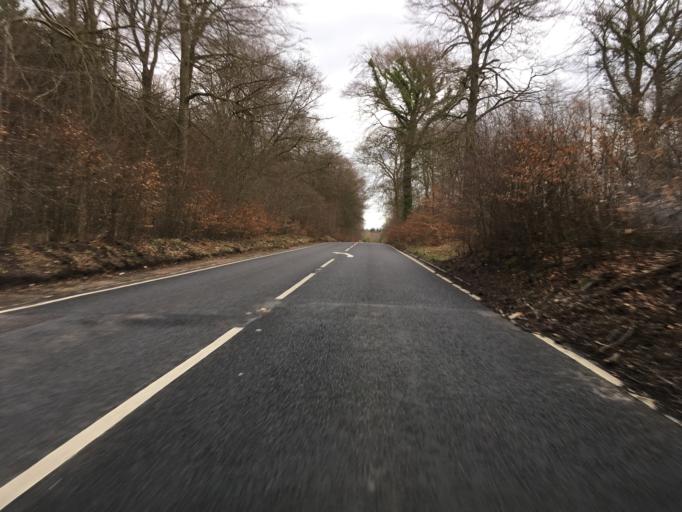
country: GB
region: England
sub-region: Gloucestershire
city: Coleford
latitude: 51.8133
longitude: -2.5975
